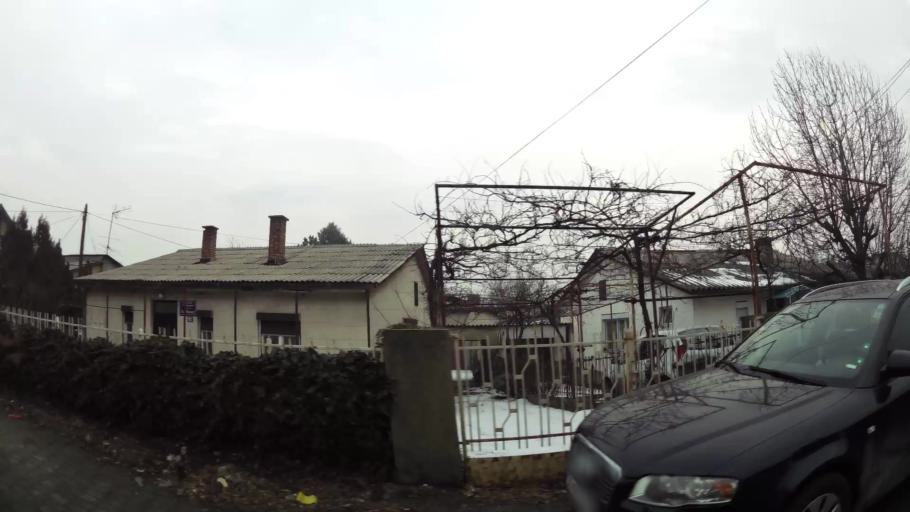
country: MK
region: Cair
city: Cair
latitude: 42.0149
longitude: 21.4565
